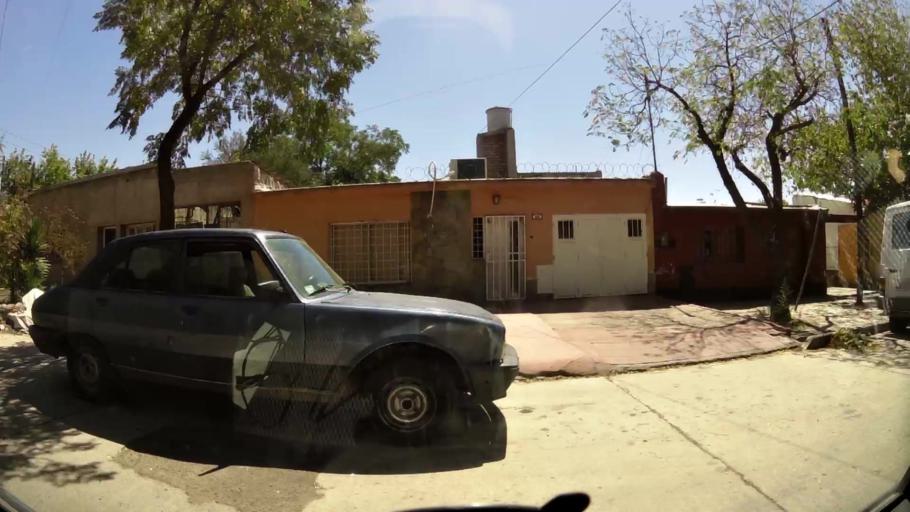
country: AR
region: Mendoza
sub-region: Departamento de Godoy Cruz
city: Godoy Cruz
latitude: -32.9154
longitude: -68.8635
